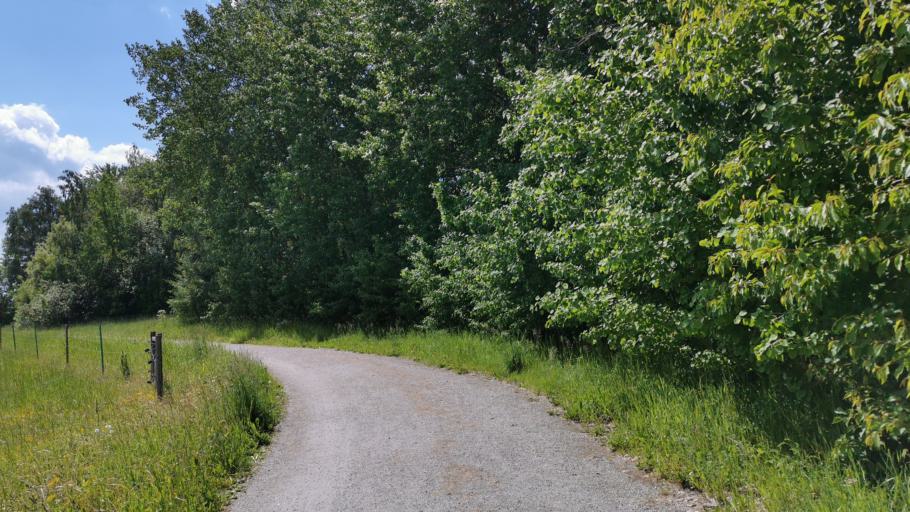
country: SE
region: OErebro
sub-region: Orebro Kommun
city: Orebro
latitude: 59.3036
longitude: 15.2109
